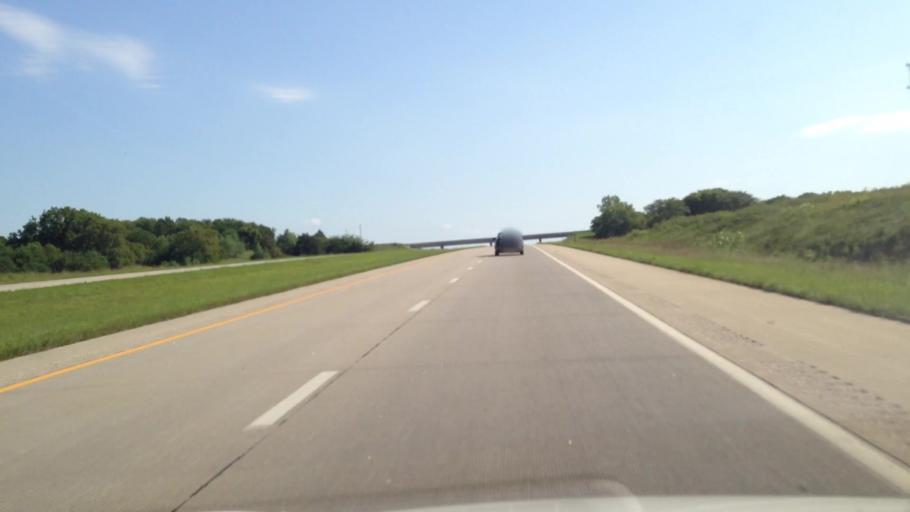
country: US
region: Kansas
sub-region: Linn County
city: Pleasanton
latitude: 38.1148
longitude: -94.7137
